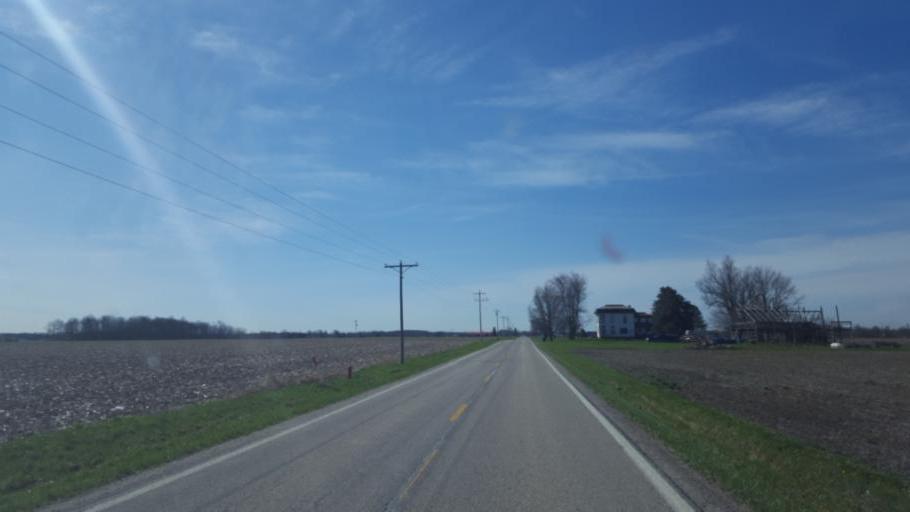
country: US
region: Ohio
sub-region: Morrow County
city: Cardington
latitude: 40.5030
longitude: -82.9630
